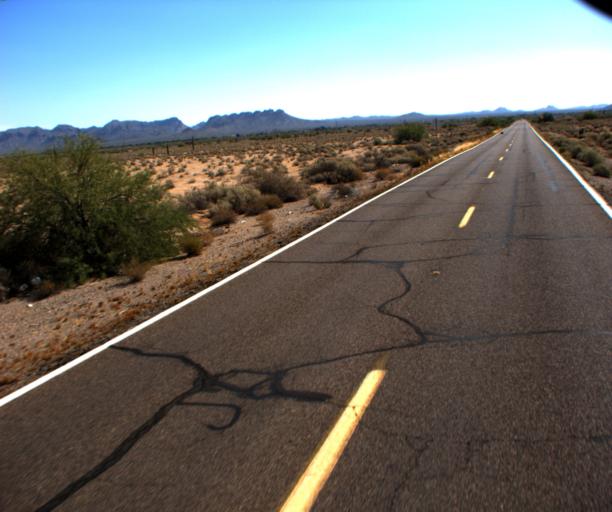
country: US
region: Arizona
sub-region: Pinal County
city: Sacaton
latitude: 33.0561
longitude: -111.6980
